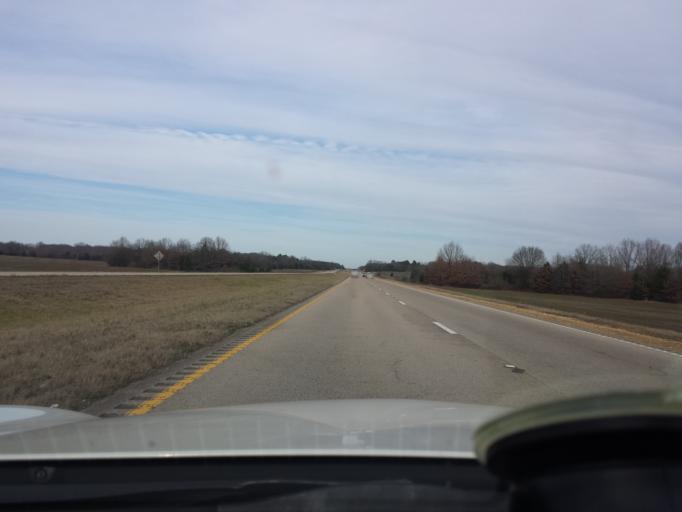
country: US
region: Mississippi
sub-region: Chickasaw County
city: Okolona
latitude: 33.9629
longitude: -88.7129
